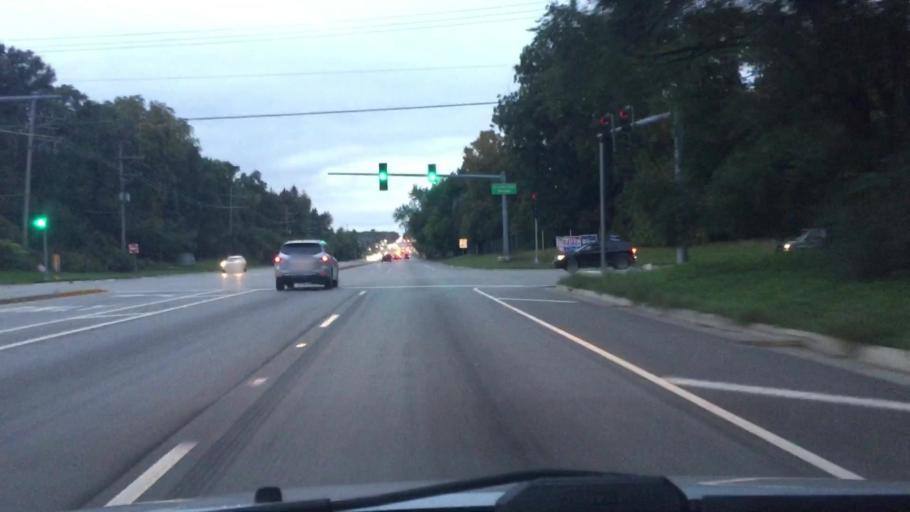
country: US
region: Illinois
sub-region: McHenry County
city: Crystal Lake
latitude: 42.2410
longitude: -88.2865
